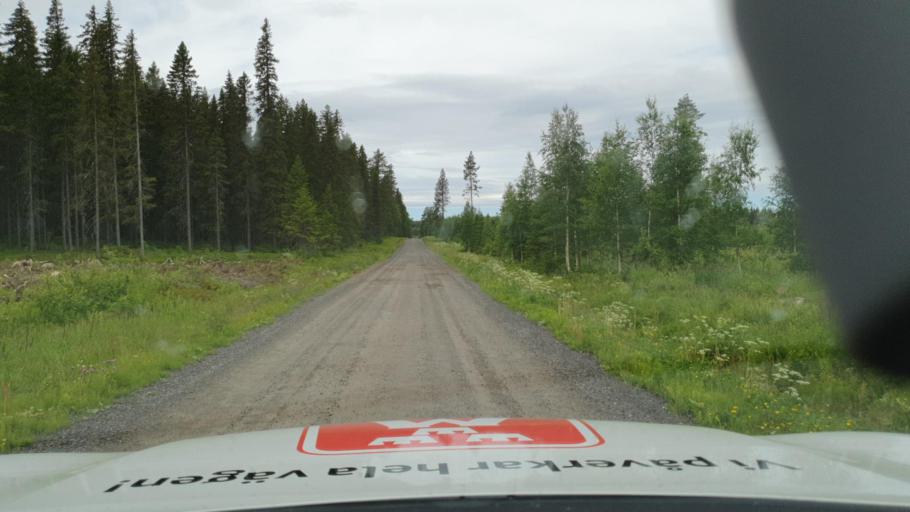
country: SE
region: Vaesterbotten
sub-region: Skelleftea Kommun
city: Burtraesk
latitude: 64.3998
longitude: 20.5629
